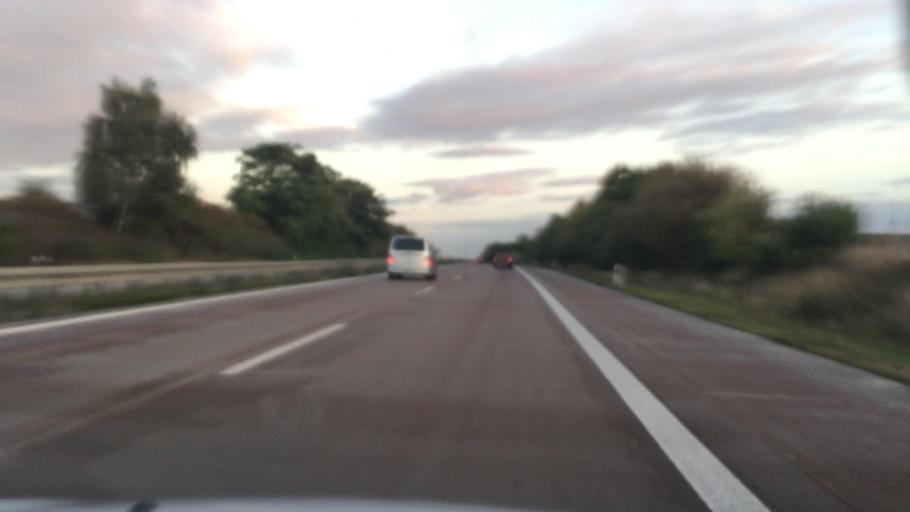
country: DE
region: Saxony
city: Ostrau
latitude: 51.2280
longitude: 12.8993
